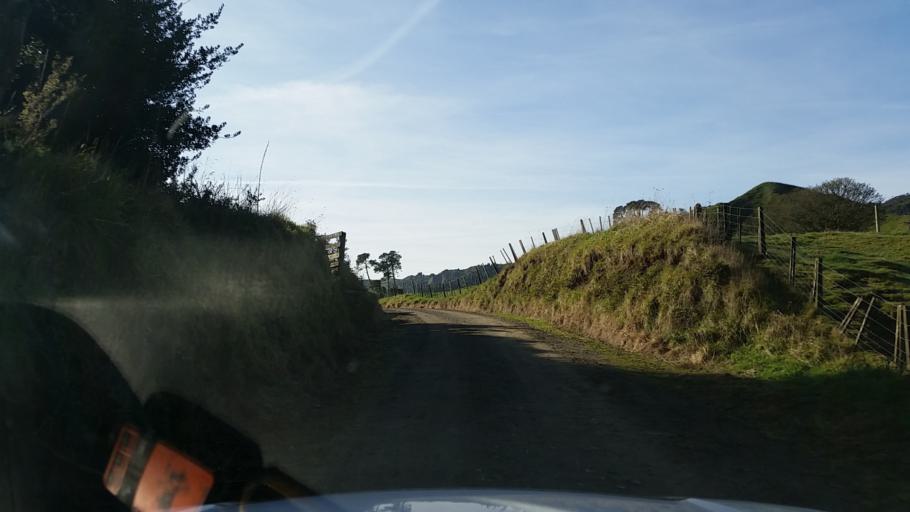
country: NZ
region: Taranaki
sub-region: South Taranaki District
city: Eltham
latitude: -39.3113
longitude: 174.5395
